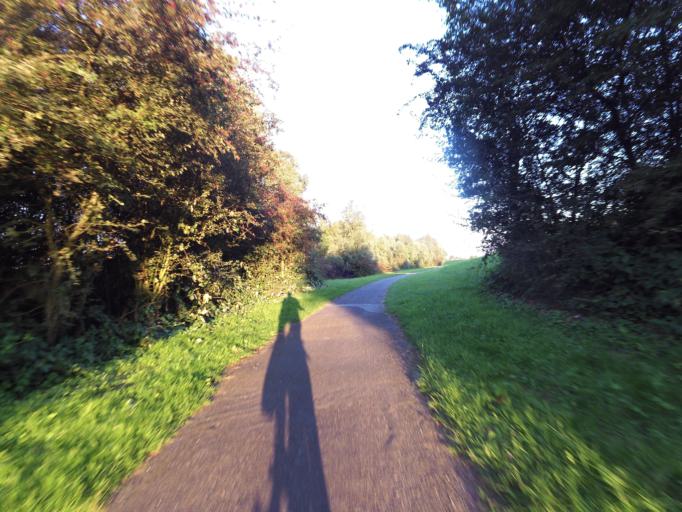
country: NL
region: Gelderland
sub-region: Gemeente Zevenaar
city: Zevenaar
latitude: 51.8607
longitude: 6.0844
